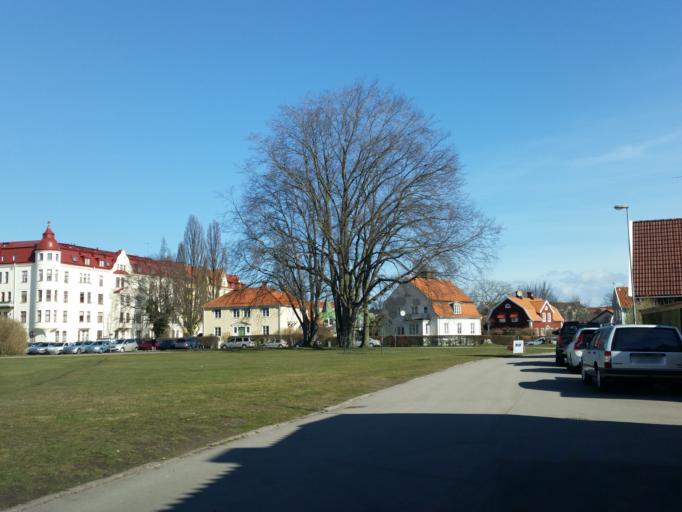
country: SE
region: Kalmar
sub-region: Kalmar Kommun
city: Kalmar
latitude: 56.6603
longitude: 16.3501
